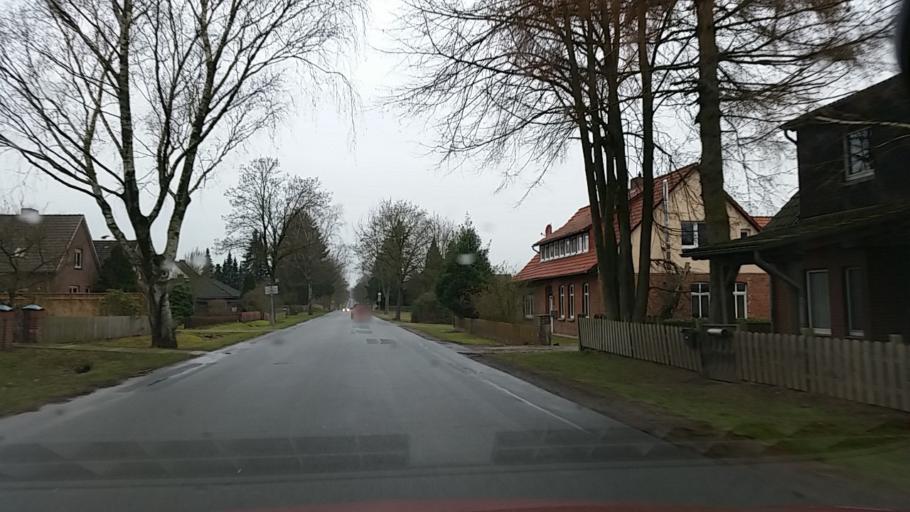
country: DE
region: Lower Saxony
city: Sprakensehl
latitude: 52.7671
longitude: 10.4866
